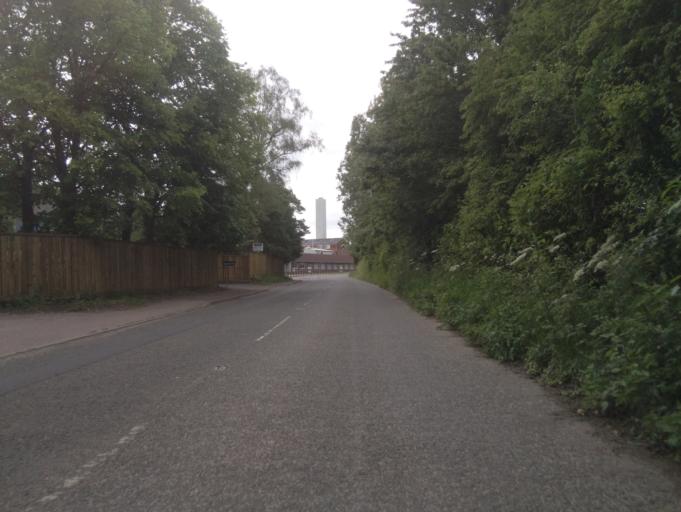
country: GB
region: England
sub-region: Herefordshire
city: Ledbury
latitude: 52.0329
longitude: -2.4436
